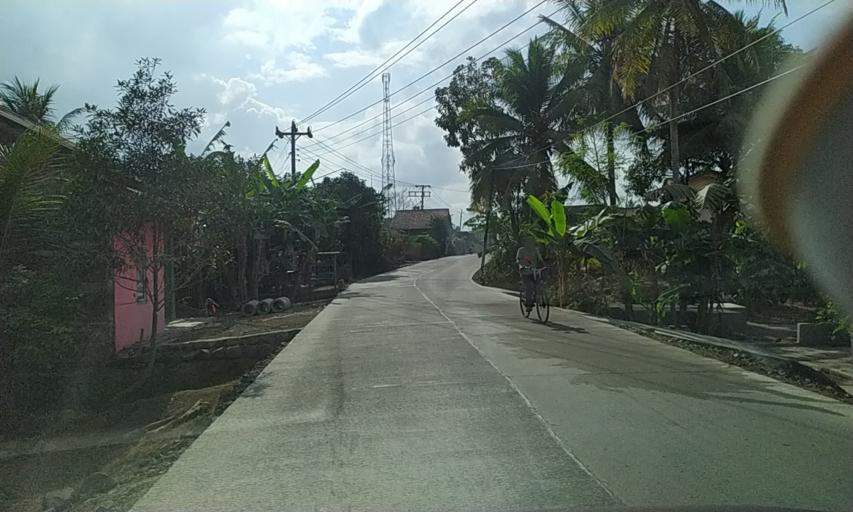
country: ID
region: Central Java
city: Madusari
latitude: -7.6218
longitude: 109.0739
